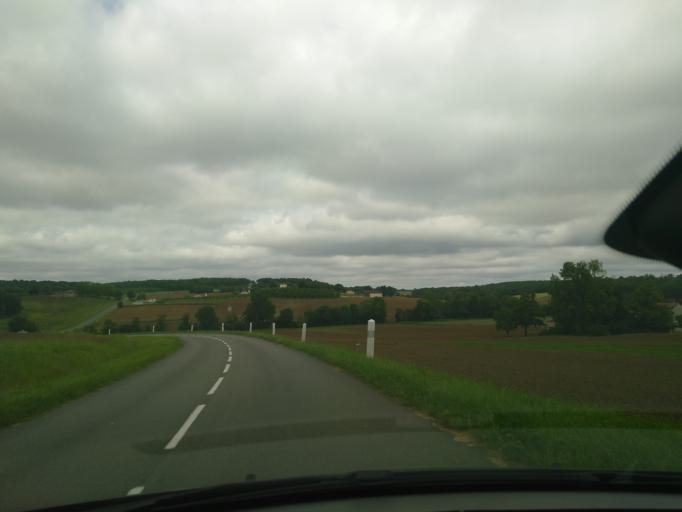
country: FR
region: Aquitaine
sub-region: Departement du Lot-et-Garonne
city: Cancon
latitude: 44.5466
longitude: 0.5755
